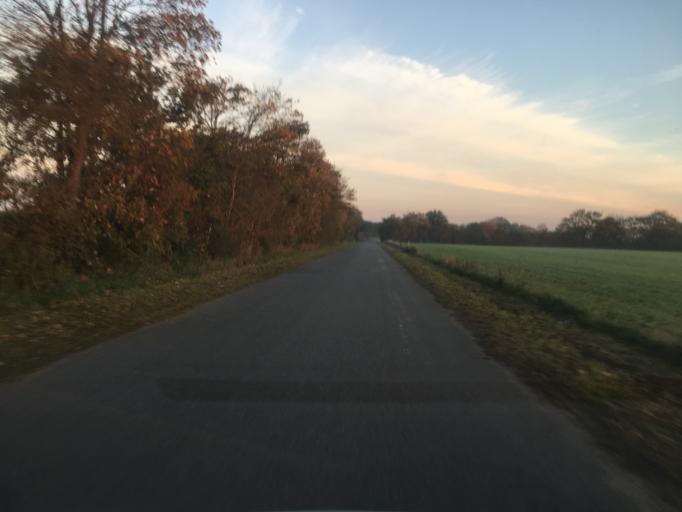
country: DK
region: South Denmark
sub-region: Tonder Kommune
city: Logumkloster
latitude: 55.0180
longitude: 9.0463
